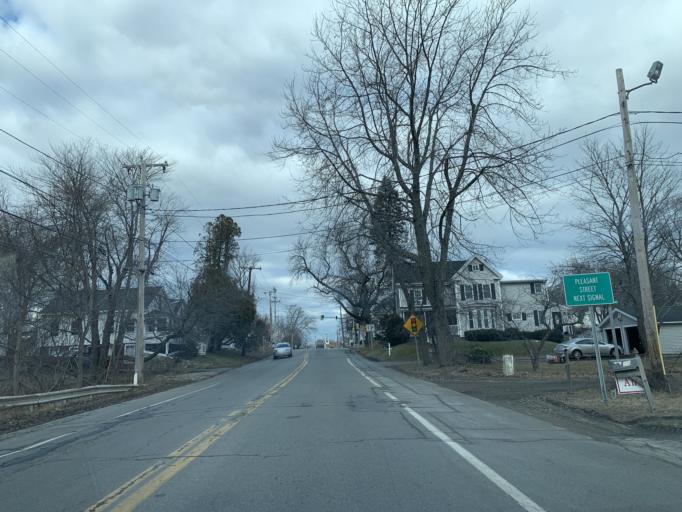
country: US
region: Massachusetts
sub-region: Essex County
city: Salisbury
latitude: 42.8382
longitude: -70.8611
